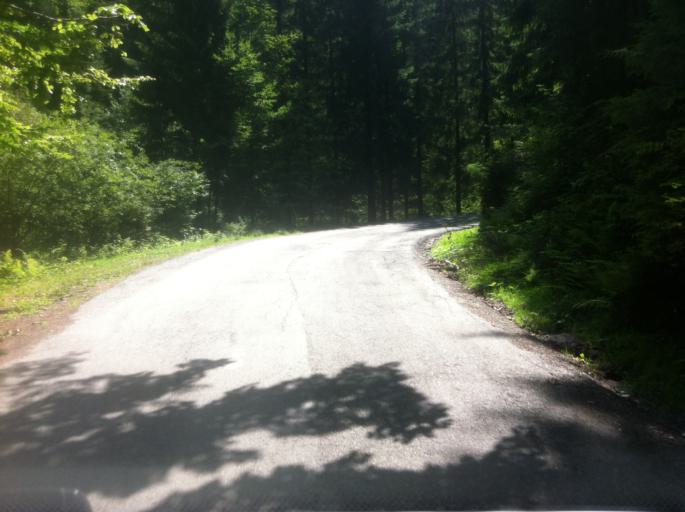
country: RO
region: Hunedoara
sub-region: Oras Petrila
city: Petrila
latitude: 45.4095
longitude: 23.5010
